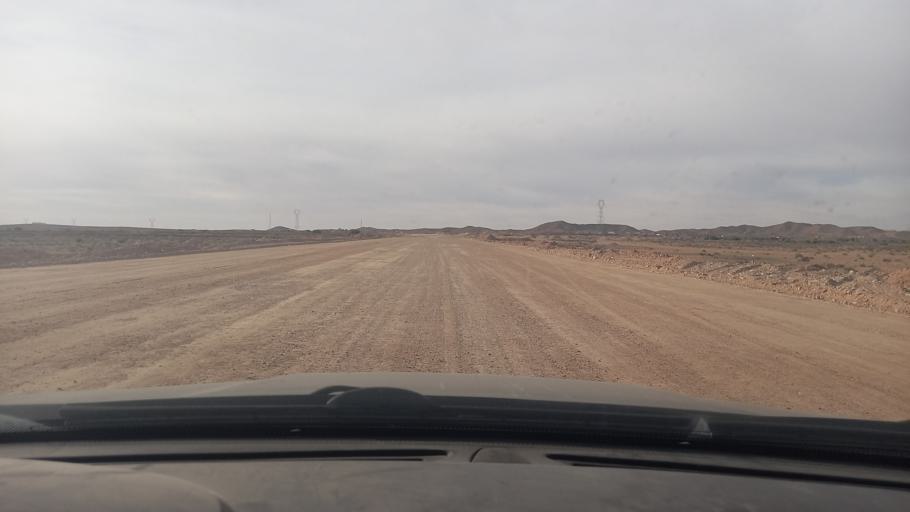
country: TN
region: Tataouine
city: Tataouine
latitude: 33.1335
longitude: 10.5034
